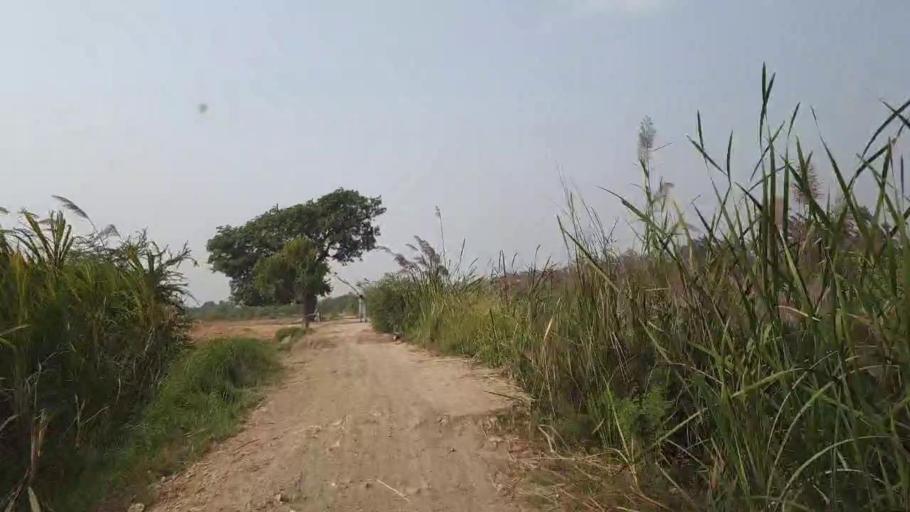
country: PK
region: Sindh
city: Matli
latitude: 25.0351
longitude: 68.5885
